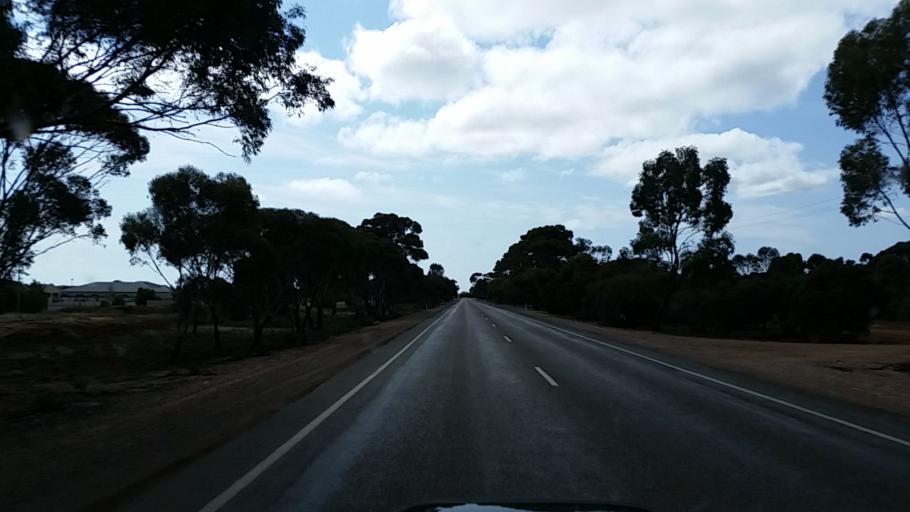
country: AU
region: South Australia
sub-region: Port Pirie City and Dists
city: Port Pirie
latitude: -33.2199
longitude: 138.0117
